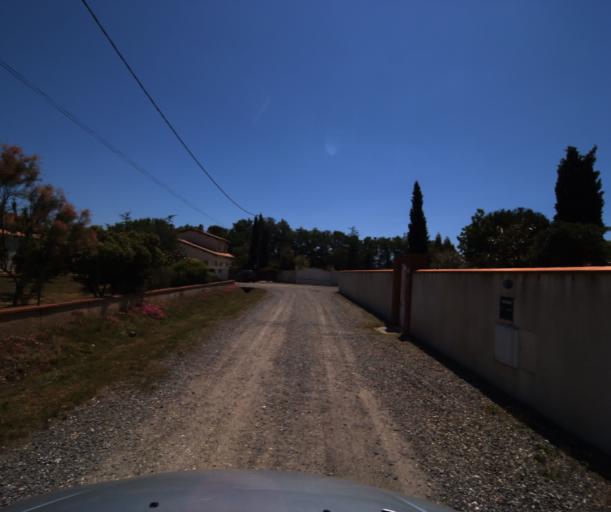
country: FR
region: Midi-Pyrenees
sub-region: Departement de la Haute-Garonne
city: Muret
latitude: 43.4523
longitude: 1.3394
